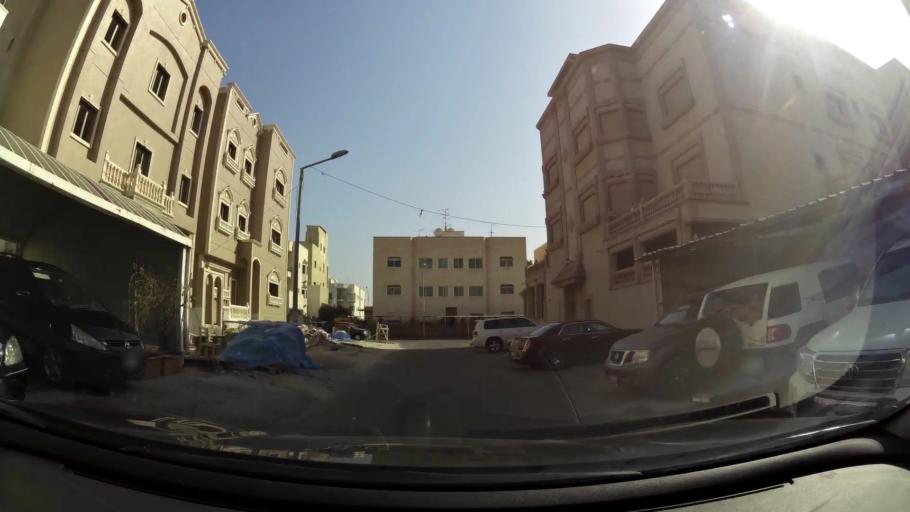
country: KW
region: Muhafazat Hawalli
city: Salwa
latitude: 29.2914
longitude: 48.0814
